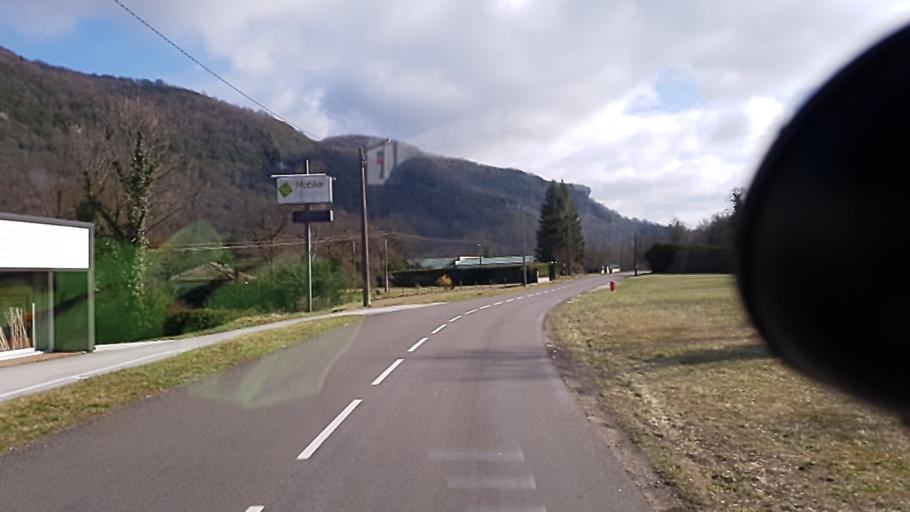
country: FR
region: Rhone-Alpes
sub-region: Departement de l'Ain
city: Dortan
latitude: 46.3394
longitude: 5.6471
